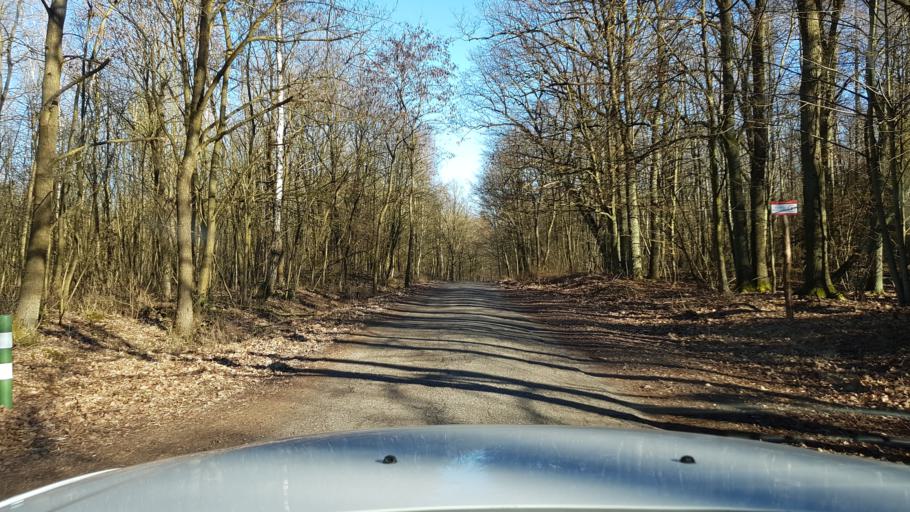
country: PL
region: West Pomeranian Voivodeship
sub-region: Powiat pyrzycki
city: Lipiany
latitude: 53.0265
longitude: 15.0149
